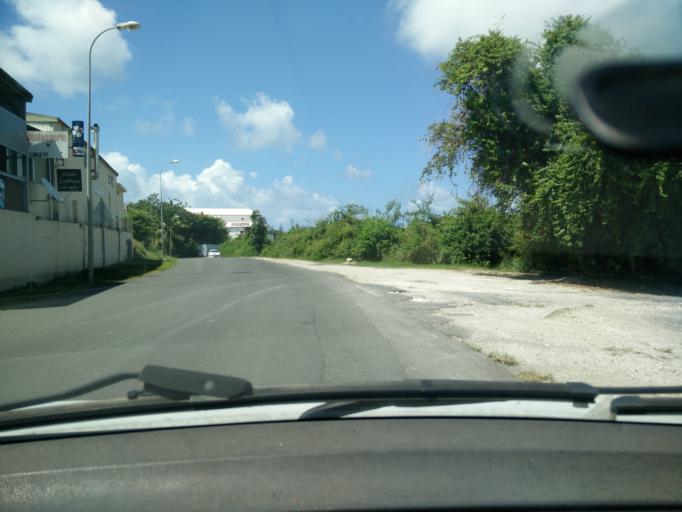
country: GP
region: Guadeloupe
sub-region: Guadeloupe
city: Le Moule
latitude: 16.3245
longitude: -61.3431
